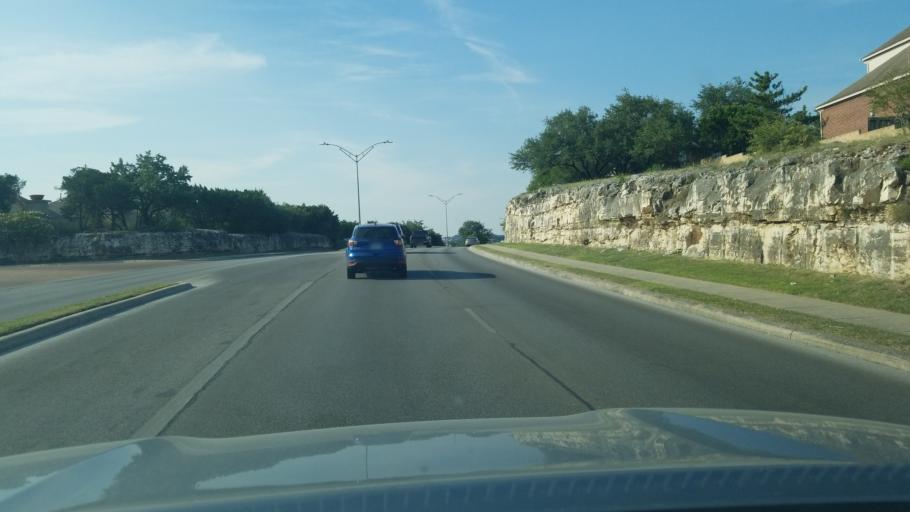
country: US
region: Texas
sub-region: Bexar County
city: Hollywood Park
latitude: 29.6409
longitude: -98.5068
